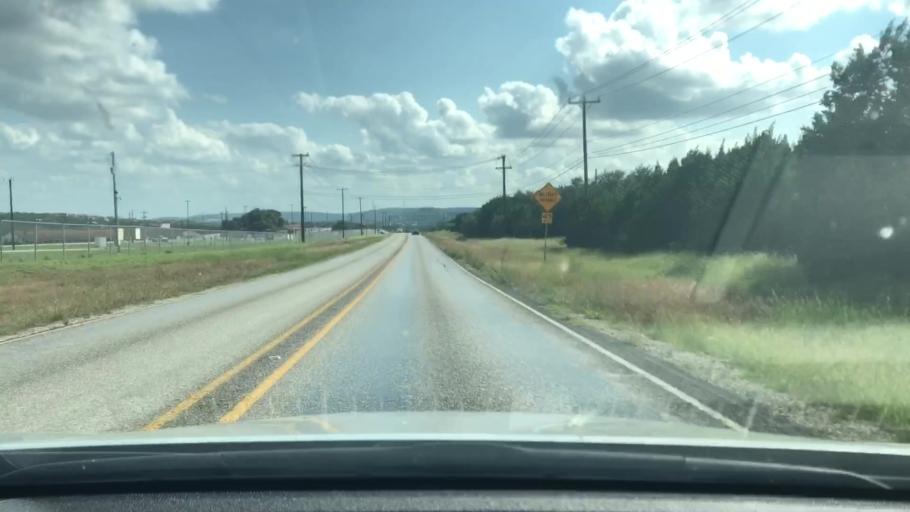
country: US
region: Texas
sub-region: Bexar County
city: Scenic Oaks
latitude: 29.6881
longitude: -98.6316
